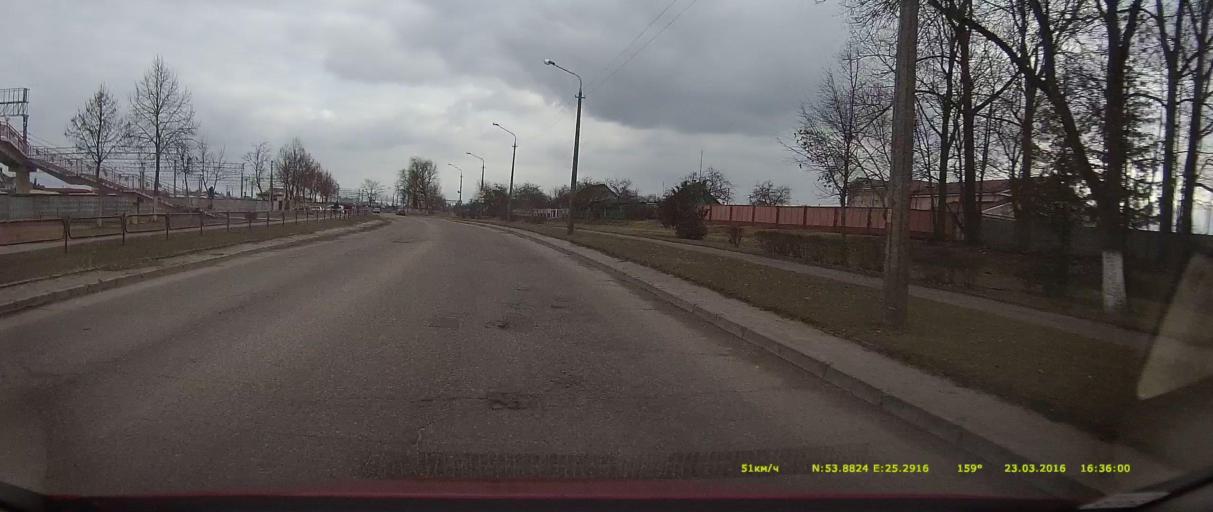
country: BY
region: Grodnenskaya
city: Lida
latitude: 53.8822
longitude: 25.2918
